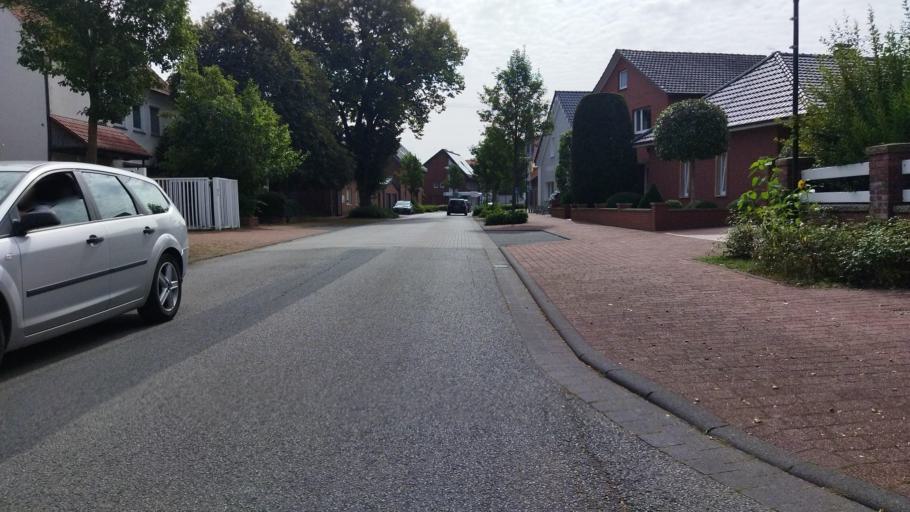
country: DE
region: Lower Saxony
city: Glandorf
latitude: 52.0846
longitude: 8.0020
